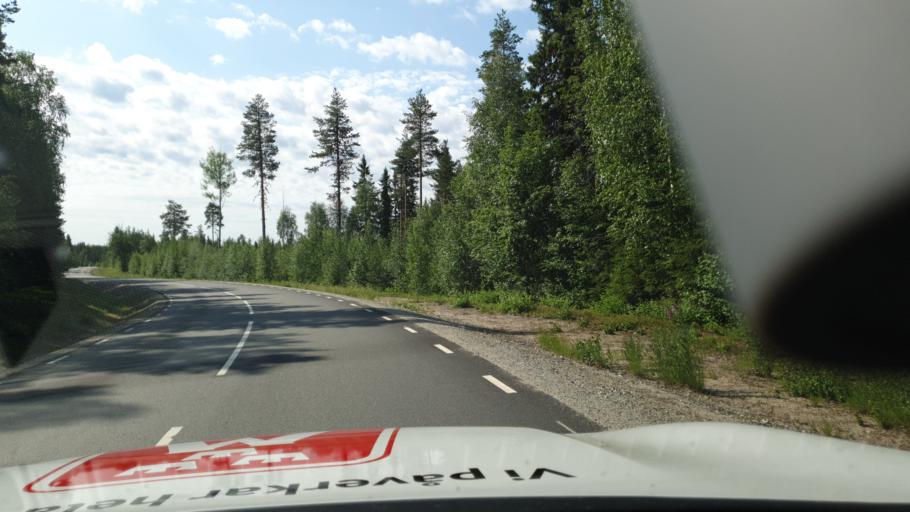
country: SE
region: Vaesterbotten
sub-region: Norsjo Kommun
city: Norsjoe
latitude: 64.6412
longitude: 19.2856
